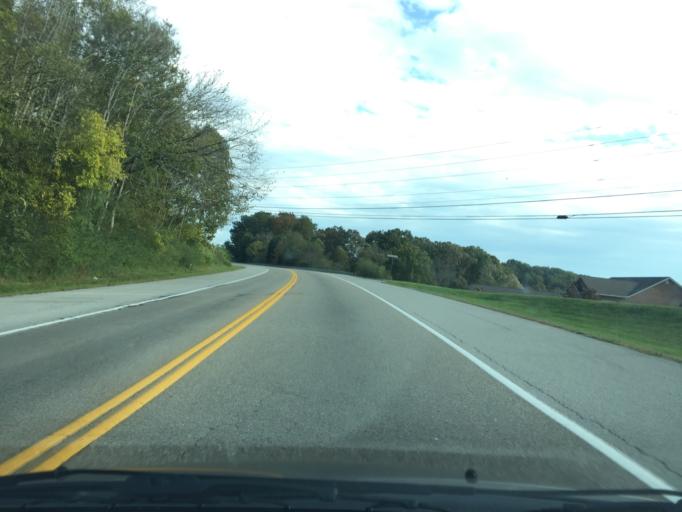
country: US
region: Tennessee
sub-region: Loudon County
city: Loudon
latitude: 35.7224
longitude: -84.3755
